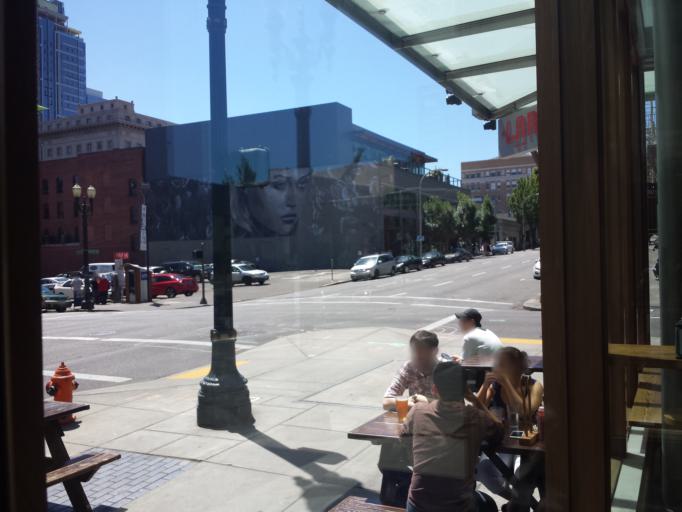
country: US
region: Oregon
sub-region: Multnomah County
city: Portland
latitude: 45.5220
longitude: -122.6832
